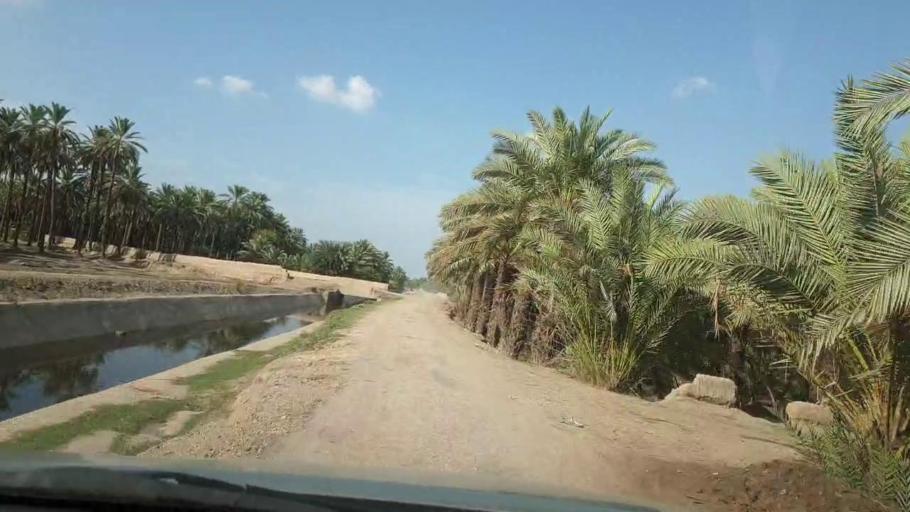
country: PK
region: Sindh
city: Sukkur
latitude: 27.6462
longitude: 68.8229
